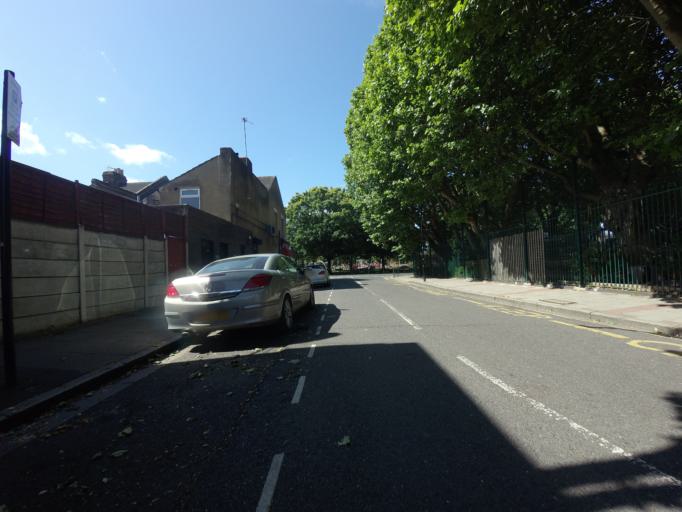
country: GB
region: England
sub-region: Greater London
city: Poplar
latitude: 51.5208
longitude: 0.0073
